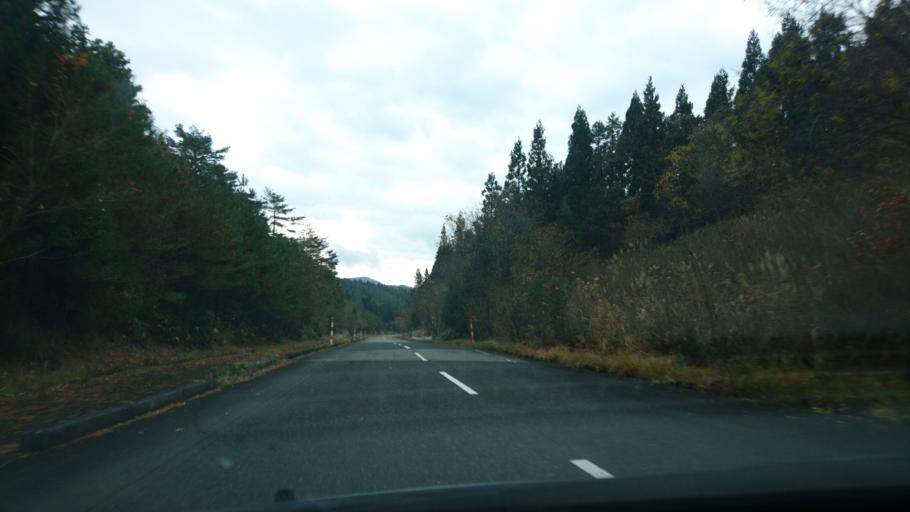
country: JP
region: Iwate
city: Ichinoseki
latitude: 38.9224
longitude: 140.9090
